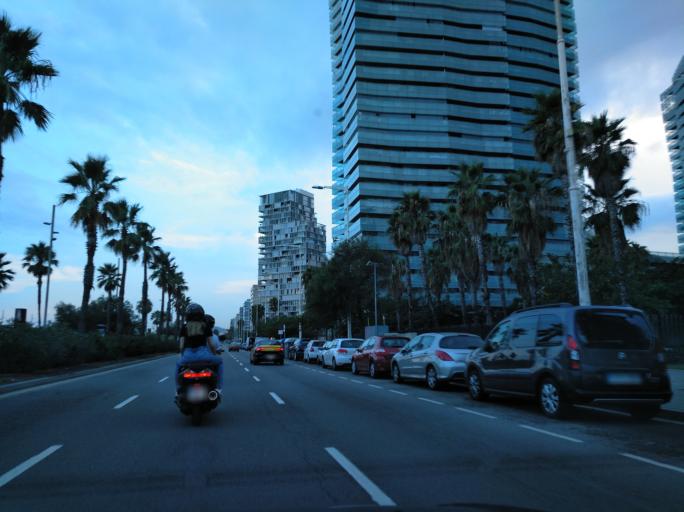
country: ES
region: Catalonia
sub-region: Provincia de Barcelona
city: Sant Marti
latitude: 41.4068
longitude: 2.2181
